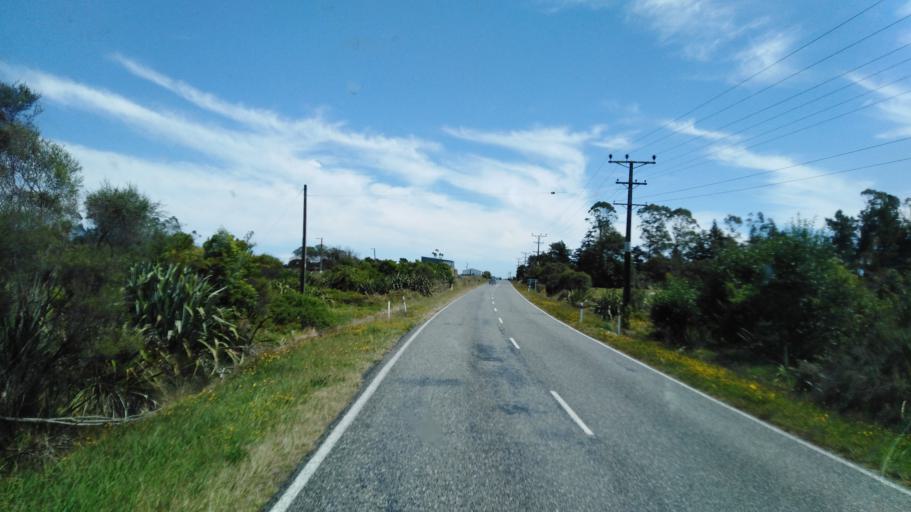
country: NZ
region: West Coast
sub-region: Buller District
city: Westport
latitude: -41.7588
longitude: 171.6518
